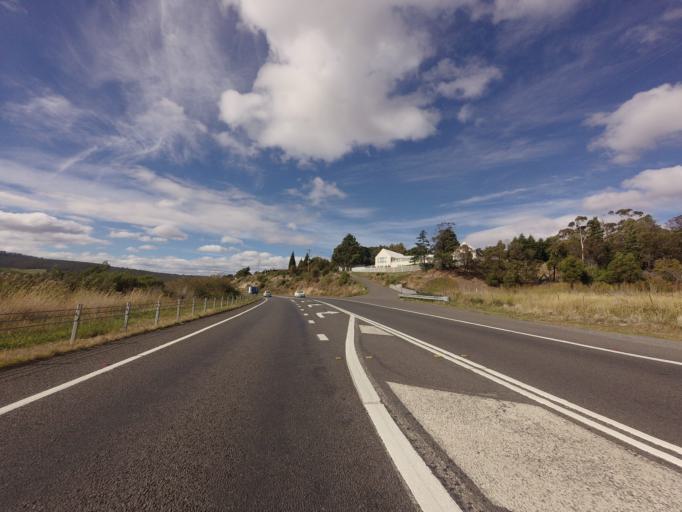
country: AU
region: Tasmania
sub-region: Brighton
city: Bridgewater
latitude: -42.7433
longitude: 147.1922
